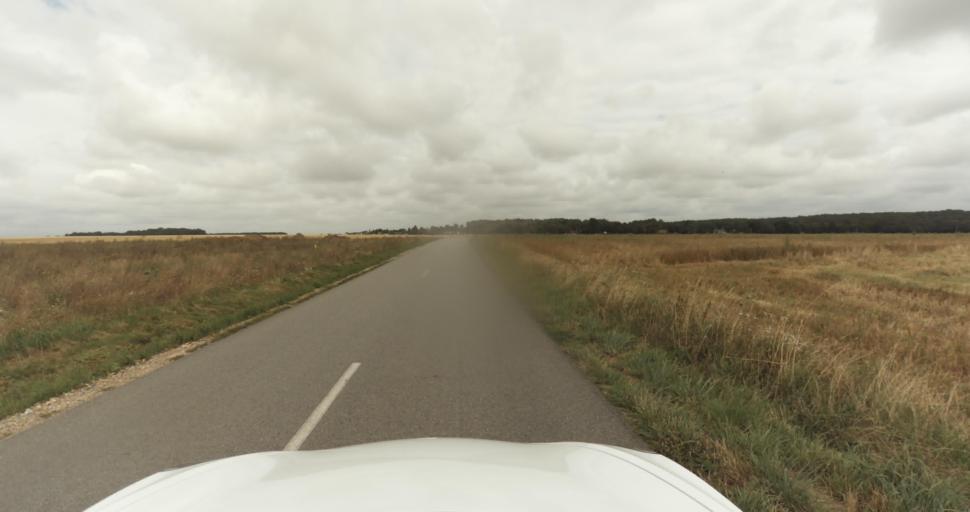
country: FR
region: Haute-Normandie
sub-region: Departement de l'Eure
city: Claville
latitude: 49.0137
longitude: 1.0340
